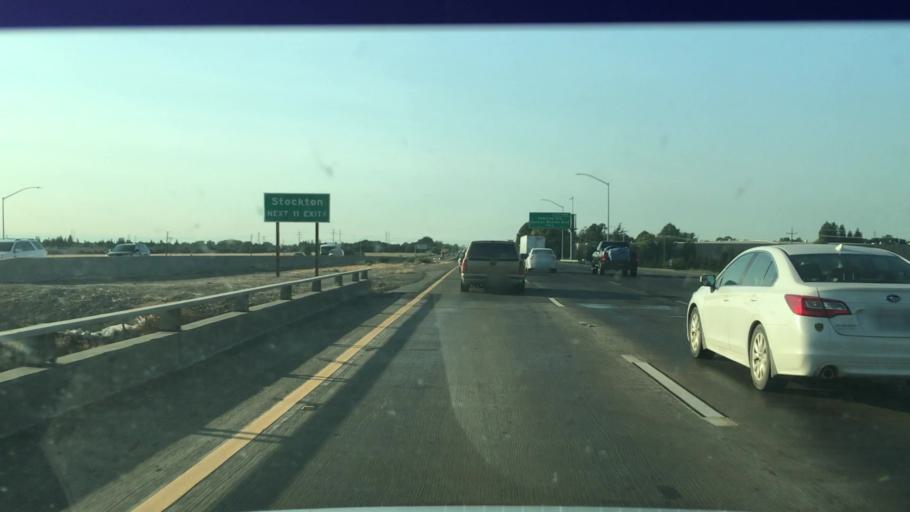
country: US
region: California
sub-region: San Joaquin County
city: Taft Mosswood
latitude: 37.8973
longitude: -121.2837
